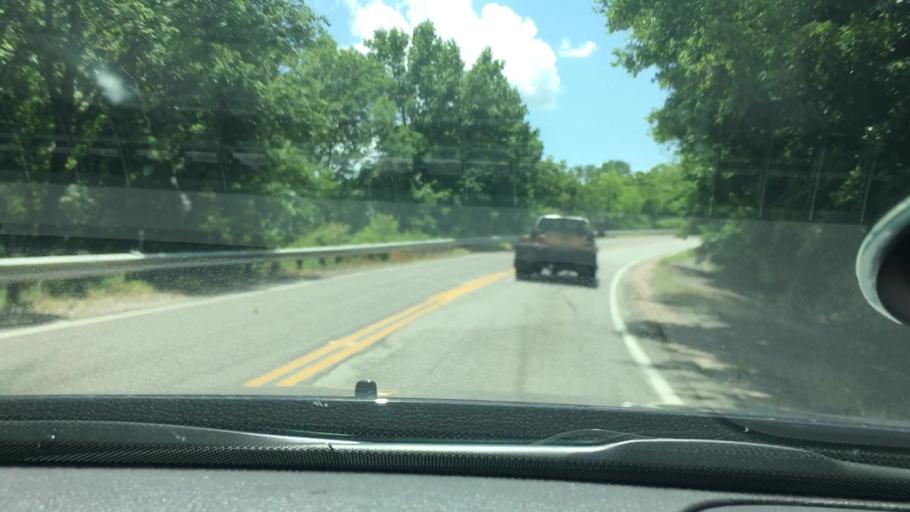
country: US
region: Oklahoma
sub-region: Pontotoc County
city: Ada
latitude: 34.5731
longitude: -96.6288
